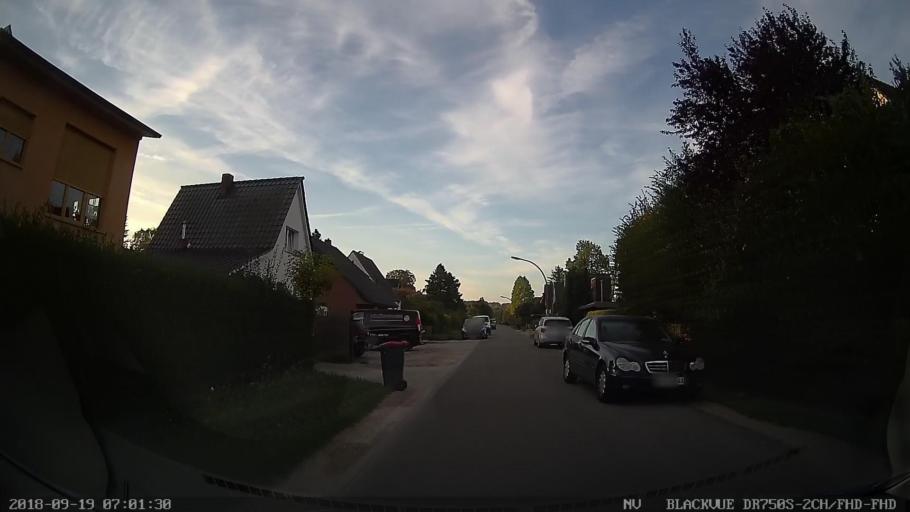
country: DE
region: Hamburg
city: Eidelstedt
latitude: 53.6293
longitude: 9.8987
